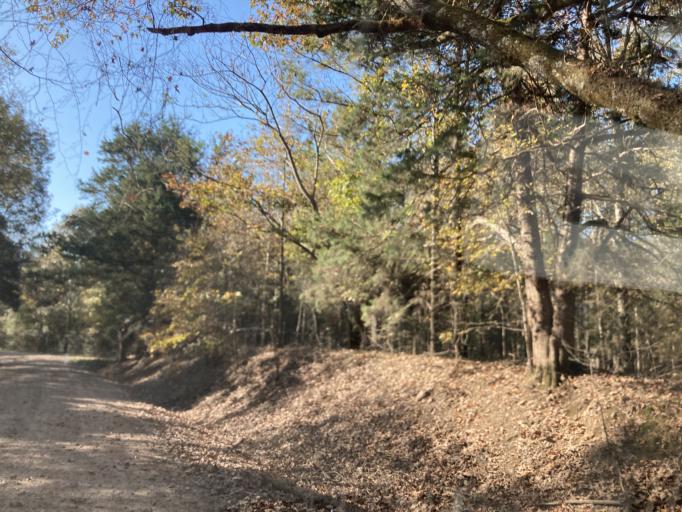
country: US
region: Mississippi
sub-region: Madison County
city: Kearney Park
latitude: 32.7336
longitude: -90.3181
